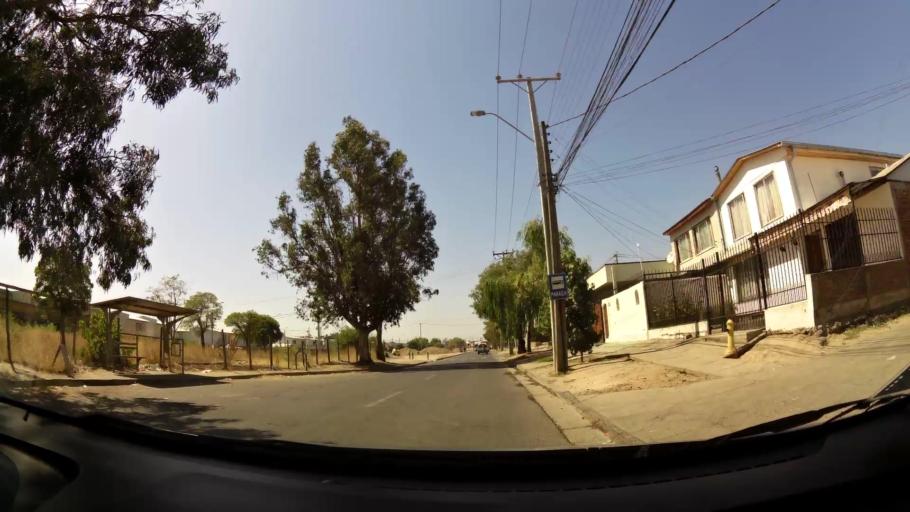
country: CL
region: Maule
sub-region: Provincia de Talca
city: Talca
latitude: -35.4162
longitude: -71.6385
